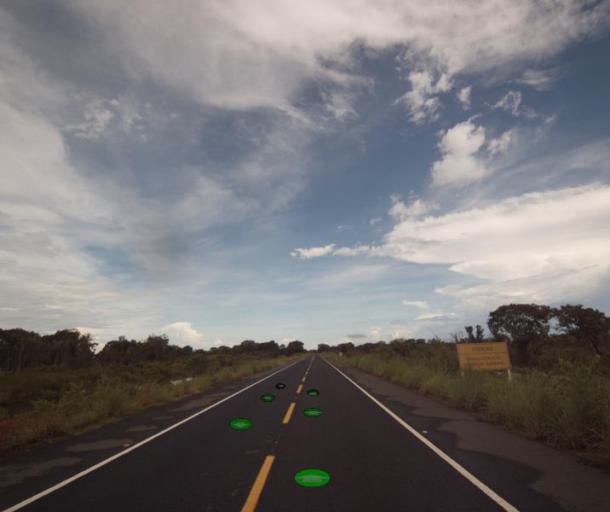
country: BR
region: Goias
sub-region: Sao Miguel Do Araguaia
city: Sao Miguel do Araguaia
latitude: -13.2278
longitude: -50.5679
